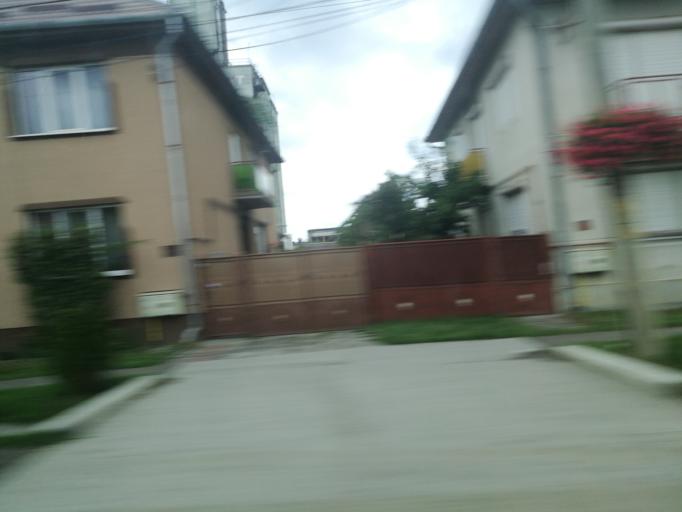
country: RO
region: Mures
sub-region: Comuna Sangeorgiu de Mures
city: Sangeorgiu de Mures
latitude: 46.5840
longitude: 24.6129
